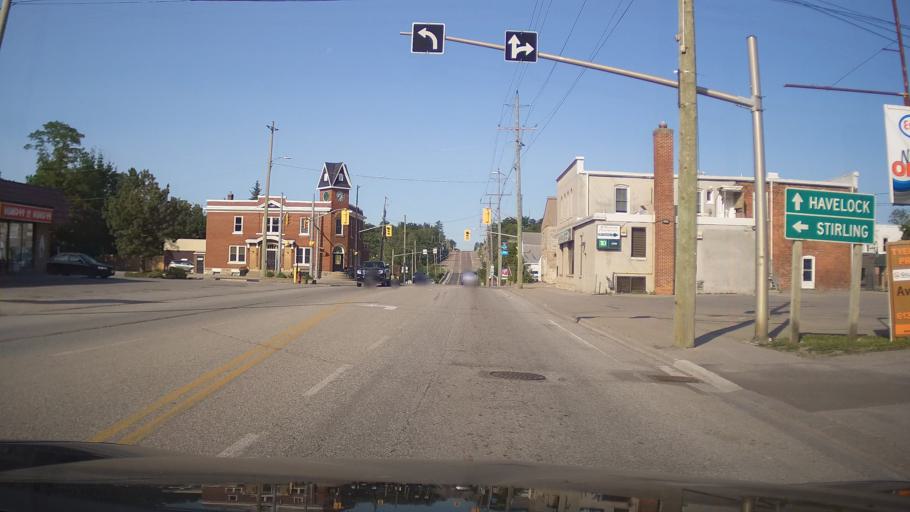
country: CA
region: Ontario
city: Quinte West
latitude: 44.4832
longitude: -77.6815
